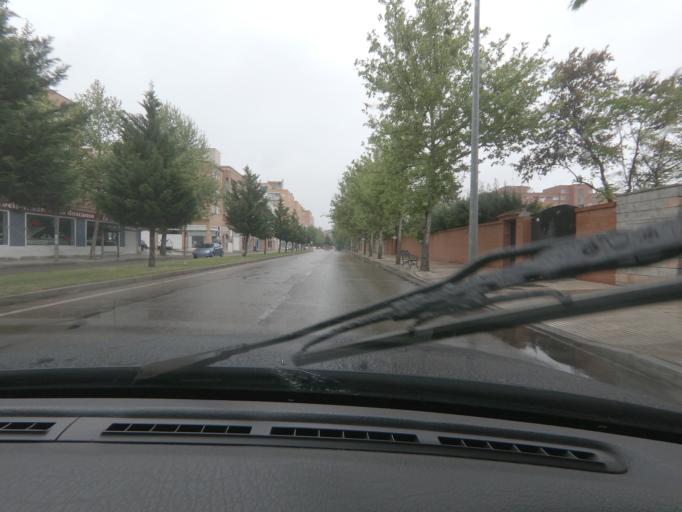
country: ES
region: Extremadura
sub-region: Provincia de Badajoz
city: Badajoz
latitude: 38.8643
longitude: -6.9726
